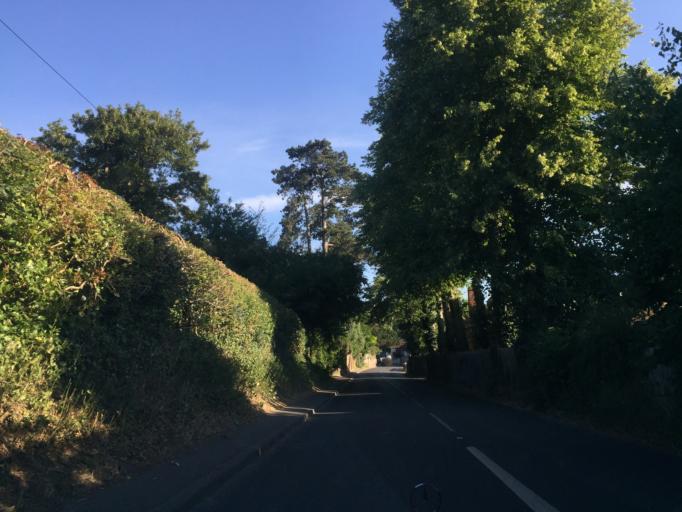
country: GB
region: England
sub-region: Wokingham
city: Wargrave
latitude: 51.5048
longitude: -0.8692
